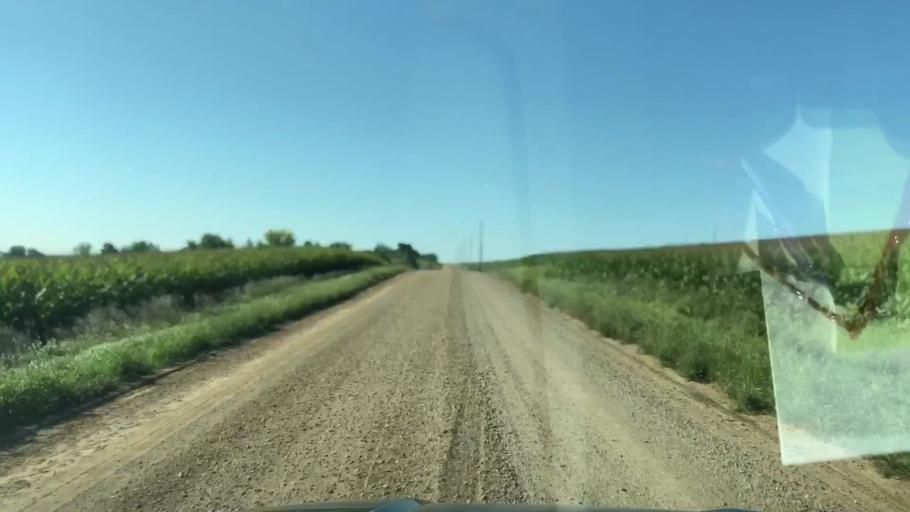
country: US
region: Iowa
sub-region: Woodbury County
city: Sergeant Bluff
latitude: 42.4643
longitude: -96.2526
